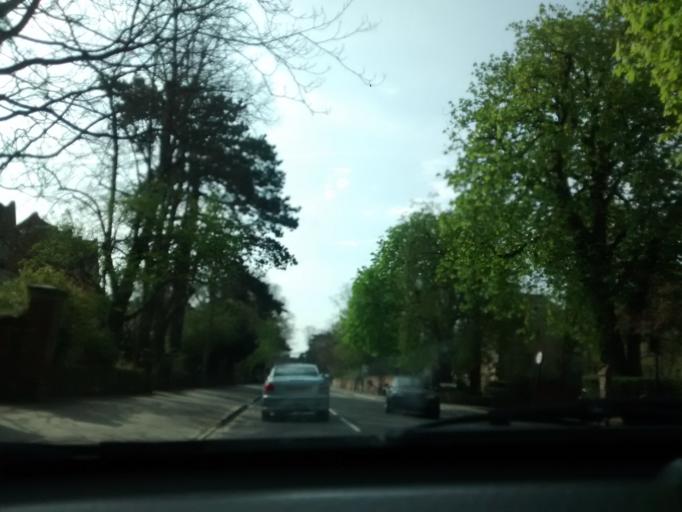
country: GB
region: England
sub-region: Oxfordshire
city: Oxford
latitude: 51.7663
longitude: -1.2652
